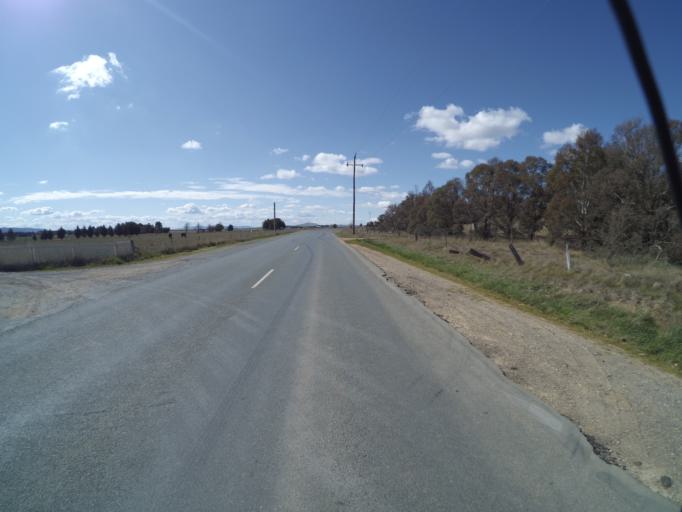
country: AU
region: New South Wales
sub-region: Palerang
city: Bungendore
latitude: -35.2330
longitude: 149.4459
